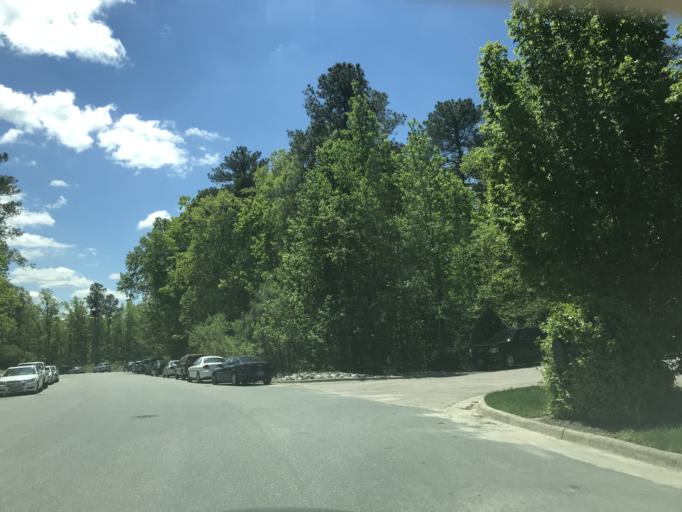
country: US
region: North Carolina
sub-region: Wake County
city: West Raleigh
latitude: 35.8808
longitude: -78.5927
